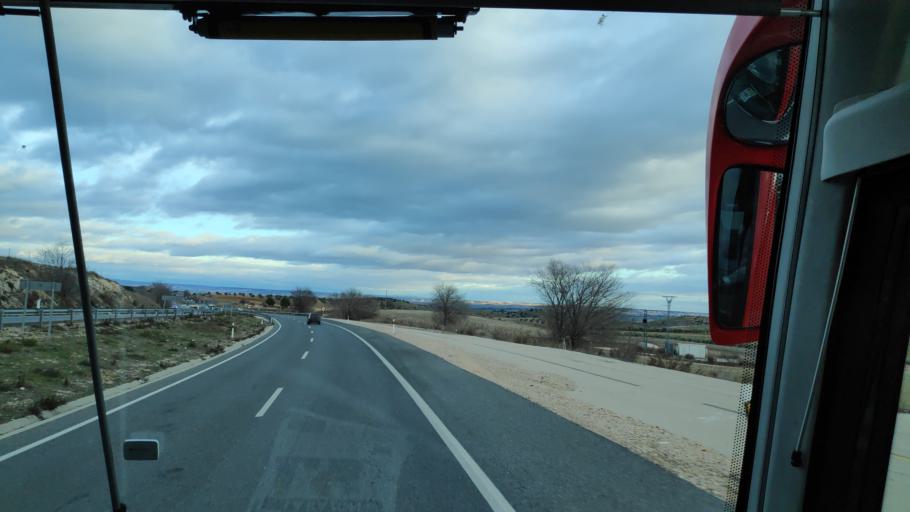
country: ES
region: Madrid
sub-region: Provincia de Madrid
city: Villarejo de Salvanes
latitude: 40.1529
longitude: -3.2488
